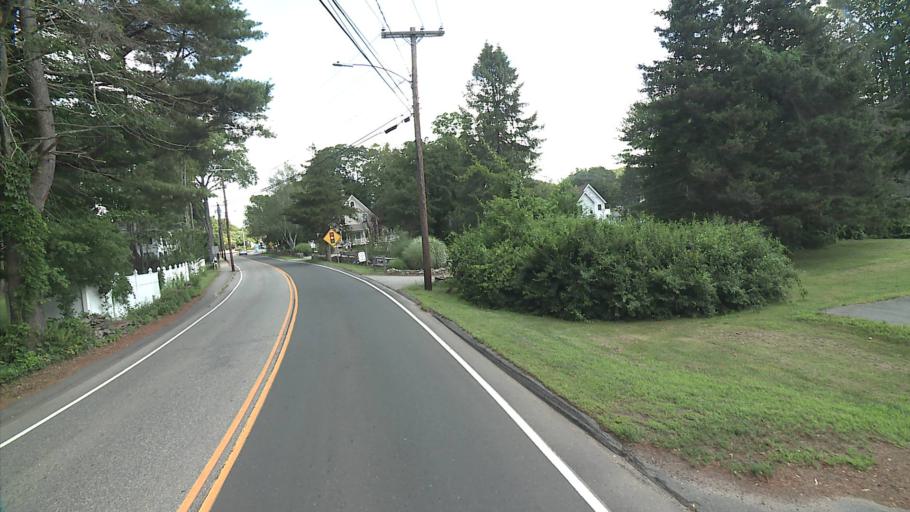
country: US
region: Connecticut
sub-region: Middlesex County
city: Essex Village
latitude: 41.3499
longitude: -72.4164
